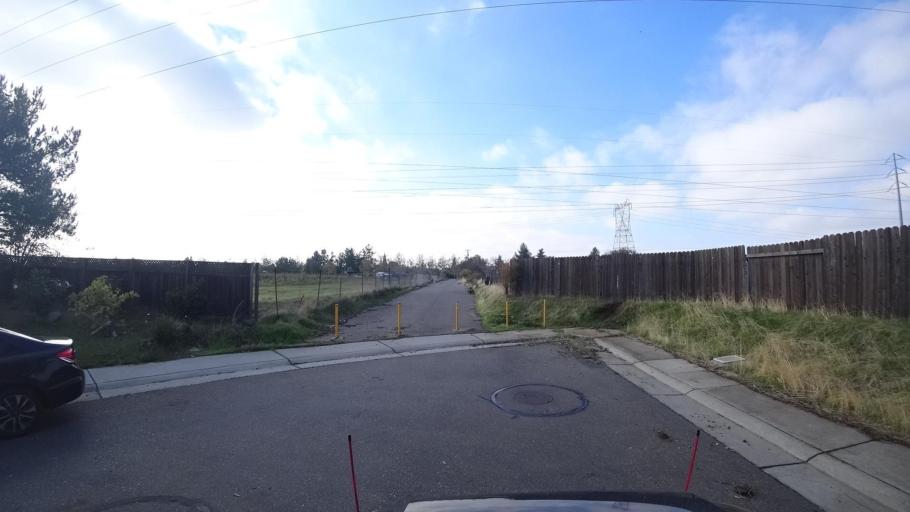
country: US
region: California
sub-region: Sacramento County
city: Vineyard
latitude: 38.4508
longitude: -121.3511
